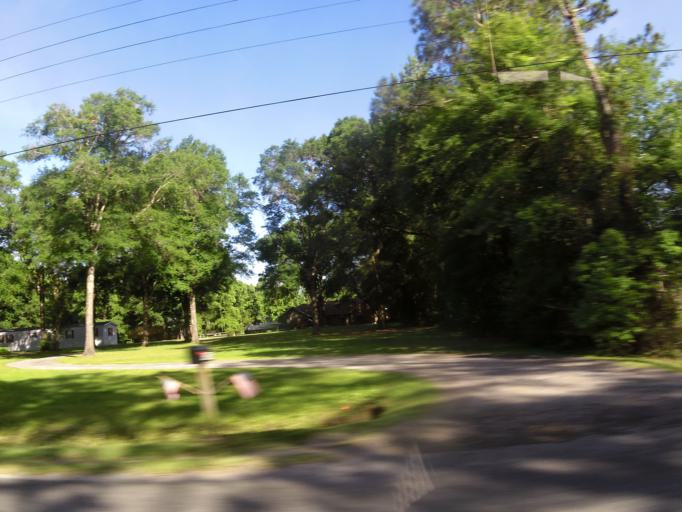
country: US
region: Florida
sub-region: Nassau County
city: Nassau Village-Ratliff
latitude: 30.4911
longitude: -81.8252
